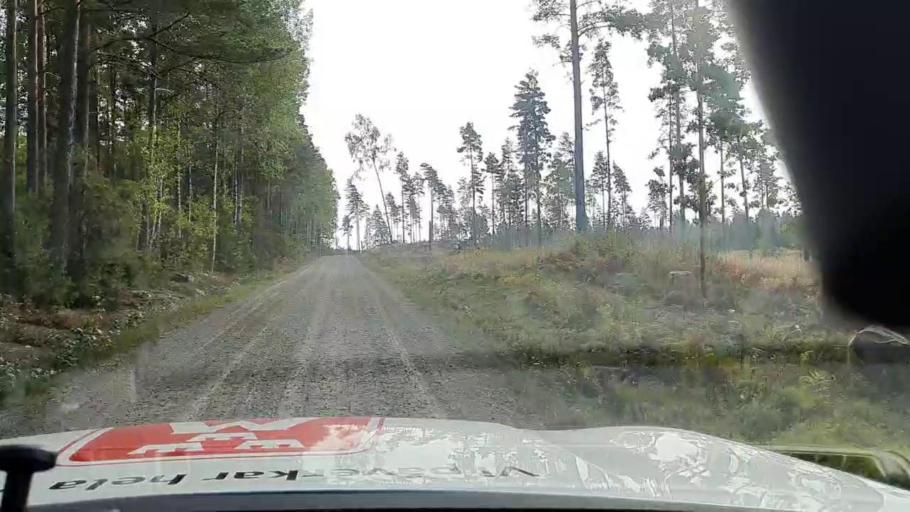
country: SE
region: Vaestmanland
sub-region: Kungsors Kommun
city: Kungsoer
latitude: 59.3577
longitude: 16.1500
